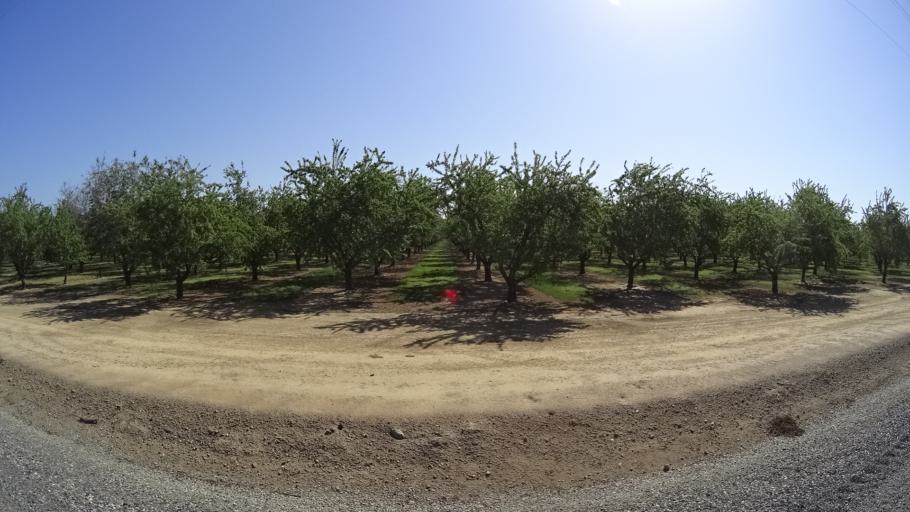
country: US
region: California
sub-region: Glenn County
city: Hamilton City
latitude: 39.6567
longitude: -122.0080
